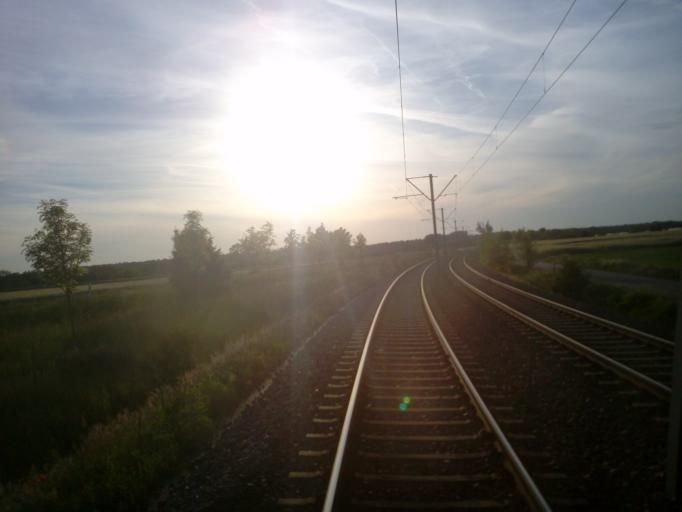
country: DE
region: Baden-Wuerttemberg
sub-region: Karlsruhe Region
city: Karlsdorf-Neuthard
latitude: 49.1115
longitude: 8.4916
